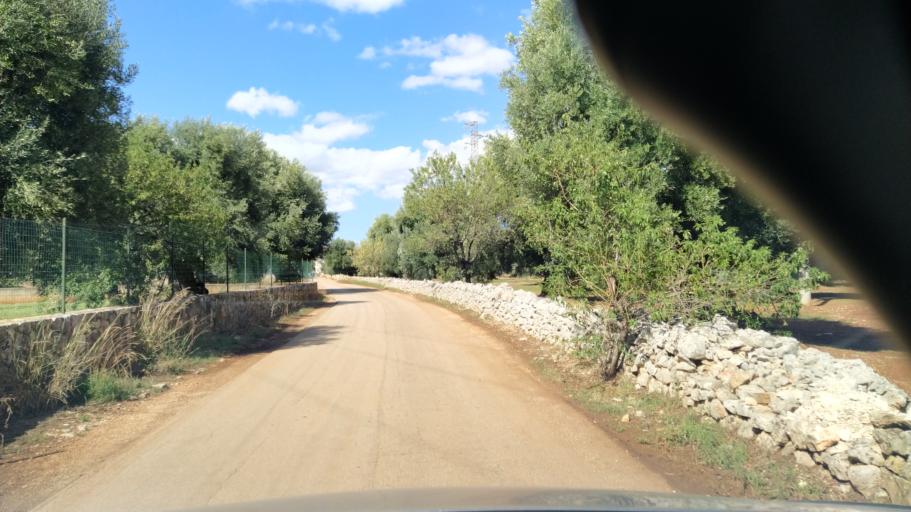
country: IT
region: Apulia
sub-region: Provincia di Brindisi
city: Fasano
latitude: 40.8242
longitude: 17.3651
